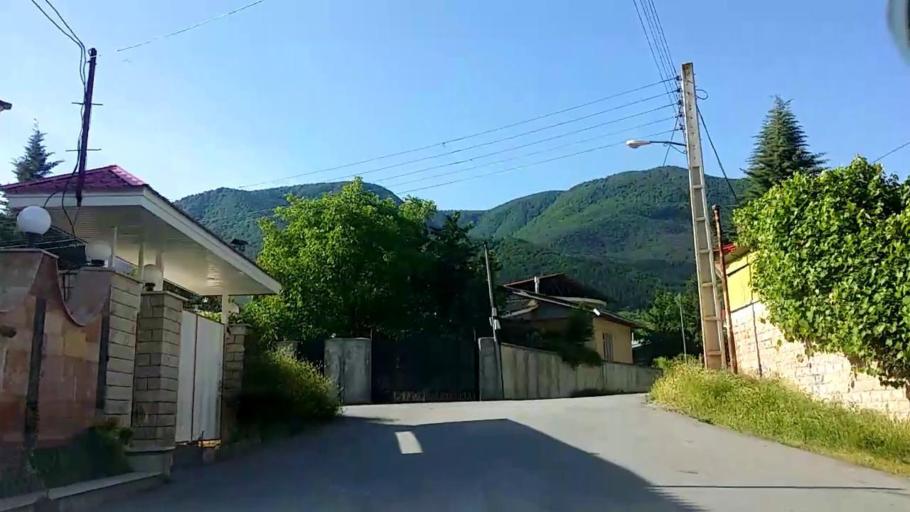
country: IR
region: Mazandaran
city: `Abbasabad
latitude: 36.5026
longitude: 51.1575
